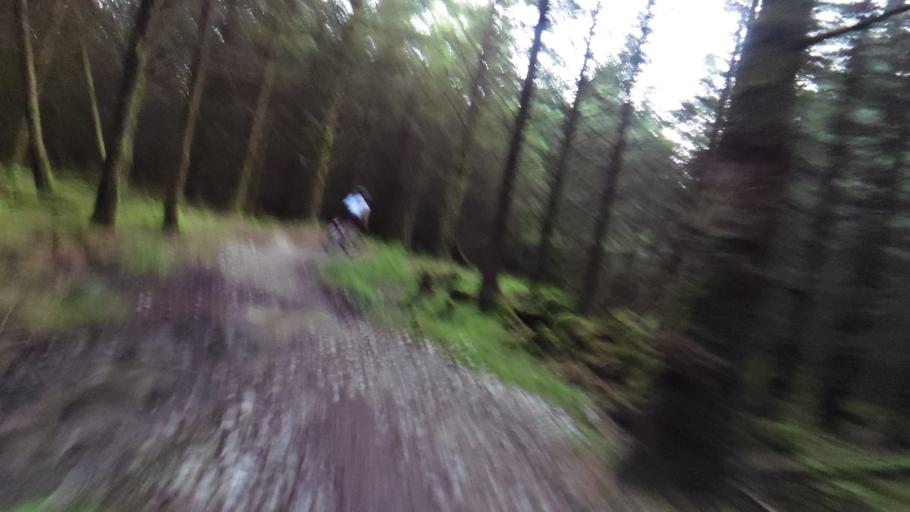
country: GB
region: England
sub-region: Lancashire
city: Clitheroe
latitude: 53.9929
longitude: -2.3861
